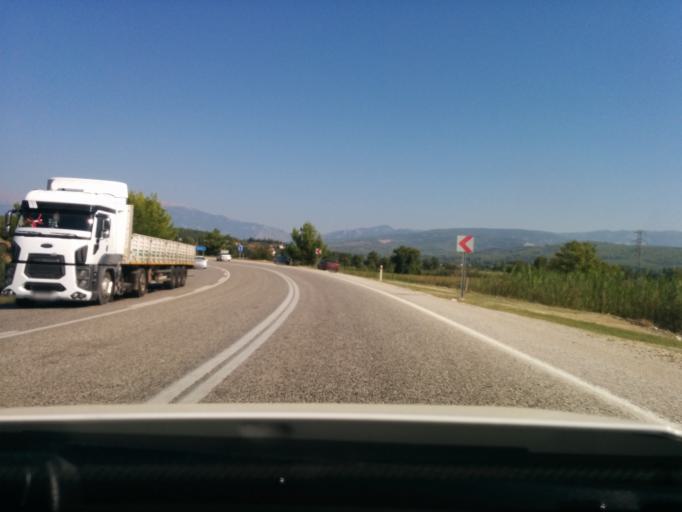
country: TR
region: Mugla
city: Kemer
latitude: 36.6250
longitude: 29.3573
